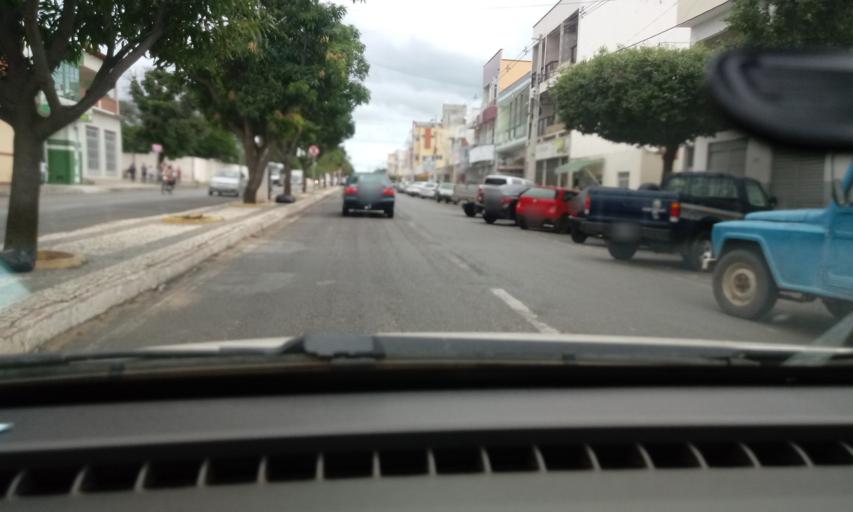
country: BR
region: Bahia
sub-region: Guanambi
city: Guanambi
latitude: -14.2175
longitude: -42.7824
